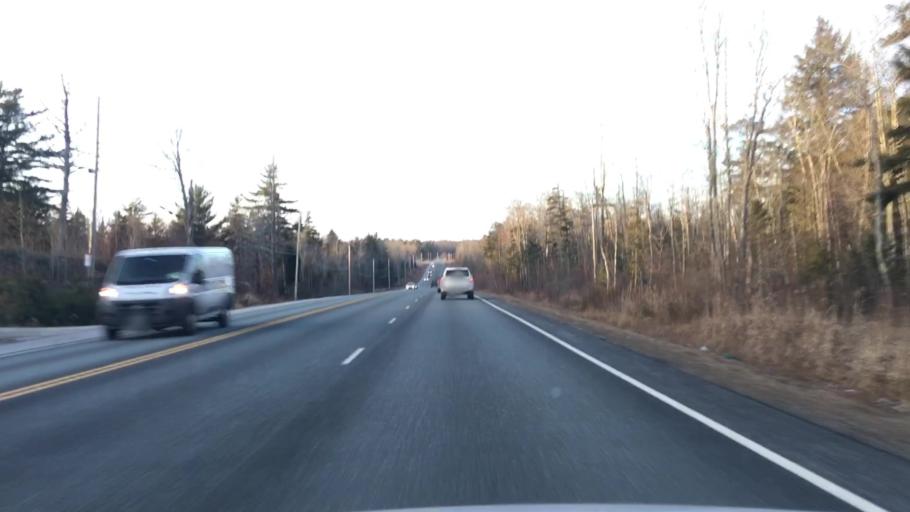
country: US
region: Maine
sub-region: Hancock County
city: Dedham
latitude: 44.6374
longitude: -68.5484
